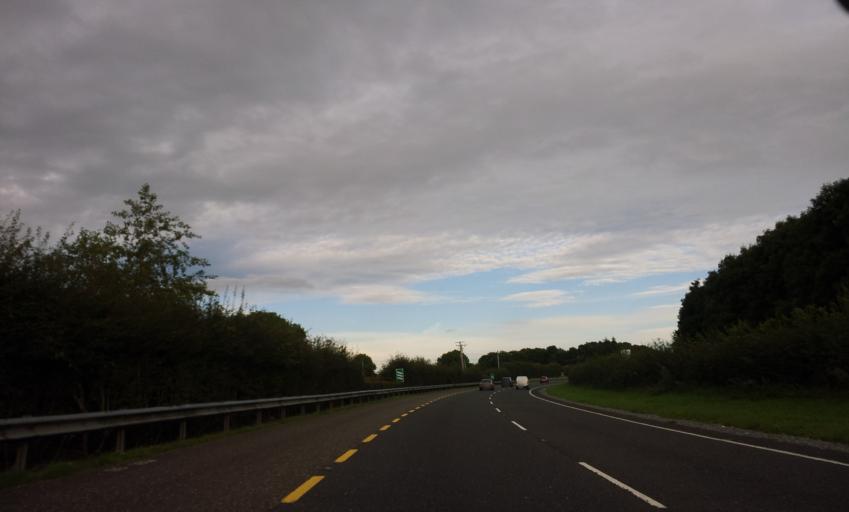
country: IE
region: Munster
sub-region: An Clar
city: Shannon
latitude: 52.7175
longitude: -8.8457
